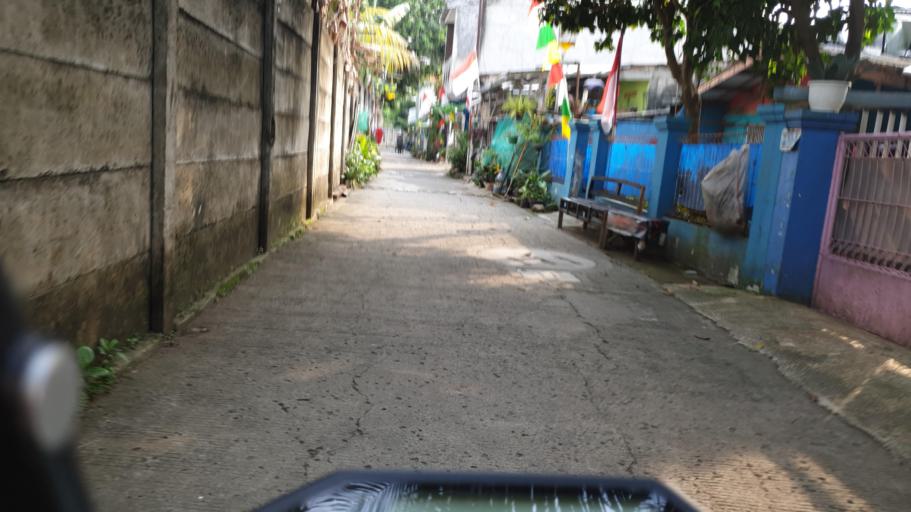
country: ID
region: West Java
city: Depok
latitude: -6.3404
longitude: 106.8301
